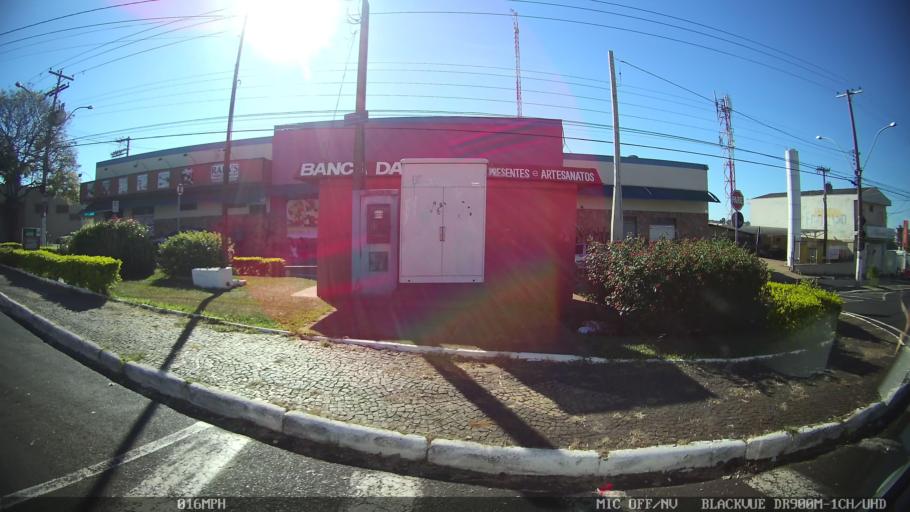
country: BR
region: Sao Paulo
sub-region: Franca
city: Franca
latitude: -20.5442
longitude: -47.4114
